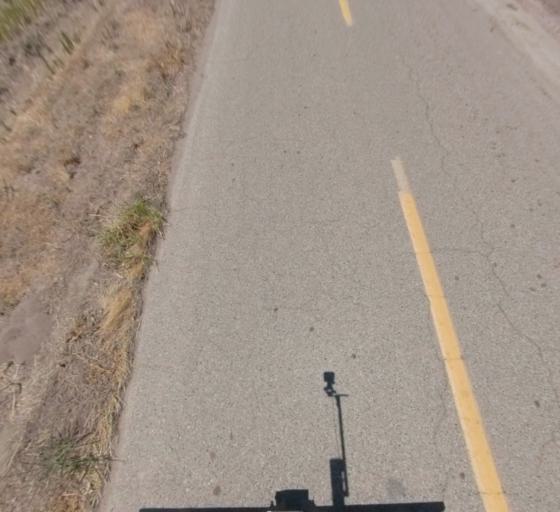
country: US
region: California
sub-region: Madera County
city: Parkwood
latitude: 36.8585
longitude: -120.1322
